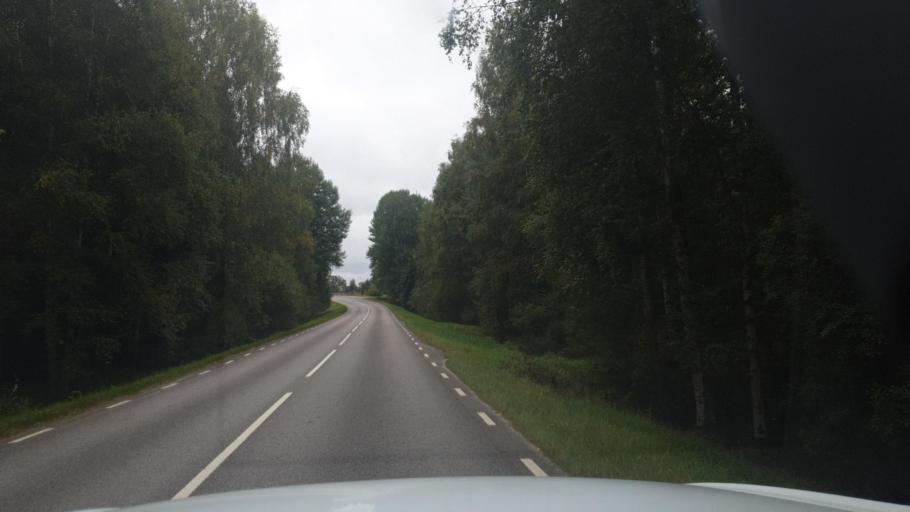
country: SE
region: Vaermland
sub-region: Sunne Kommun
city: Sunne
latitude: 59.7999
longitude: 13.0532
